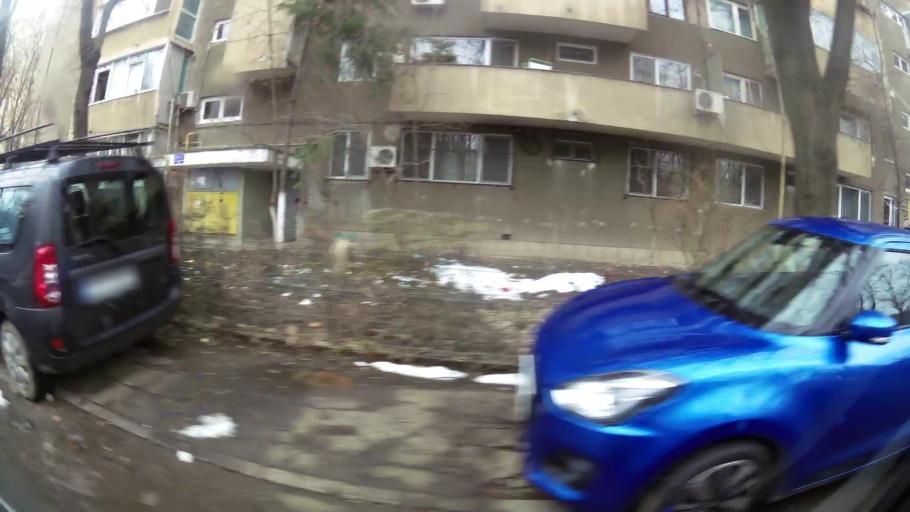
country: RO
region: Ilfov
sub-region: Comuna Chiajna
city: Rosu
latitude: 44.4249
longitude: 26.0302
